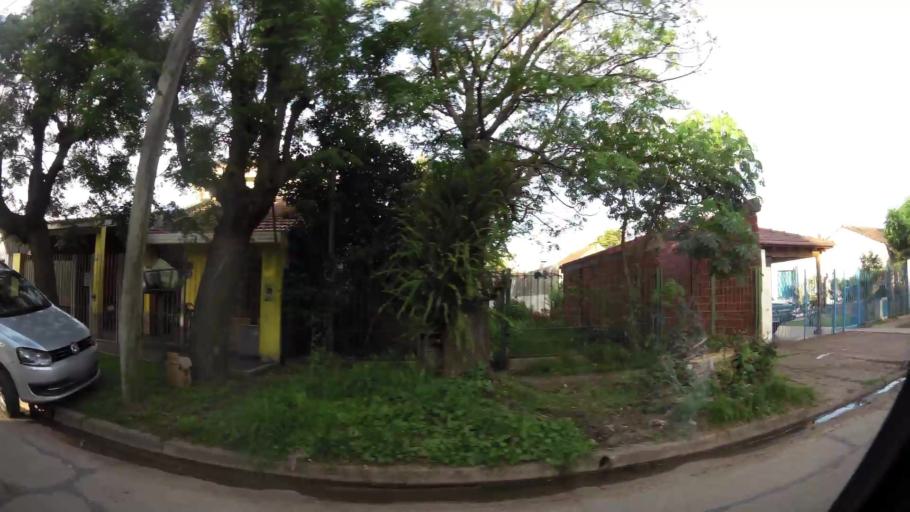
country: AR
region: Buenos Aires
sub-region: Partido de Almirante Brown
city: Adrogue
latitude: -34.7968
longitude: -58.3524
